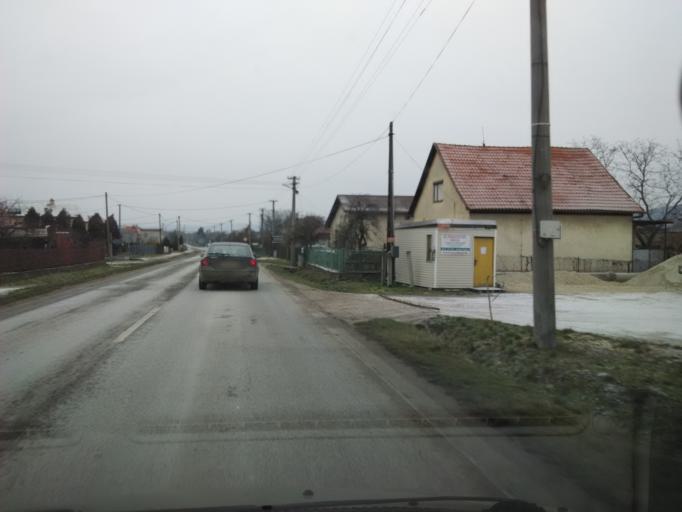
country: SK
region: Nitriansky
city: Novaky
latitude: 48.6489
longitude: 18.4947
